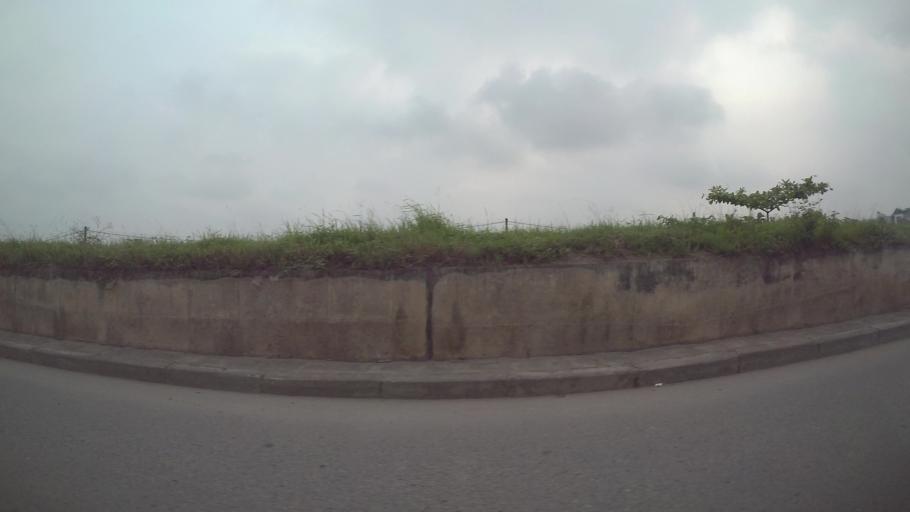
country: VN
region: Ha Noi
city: Trau Quy
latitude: 21.0750
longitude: 105.9143
